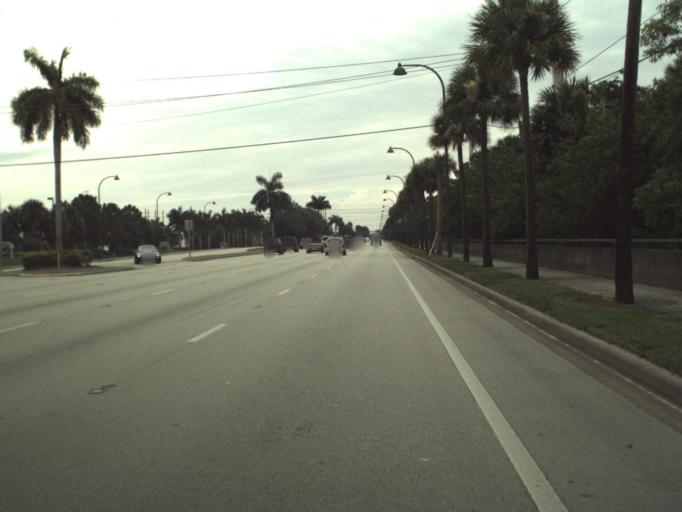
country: US
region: Florida
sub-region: Palm Beach County
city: Wellington
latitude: 26.6810
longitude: -80.2271
